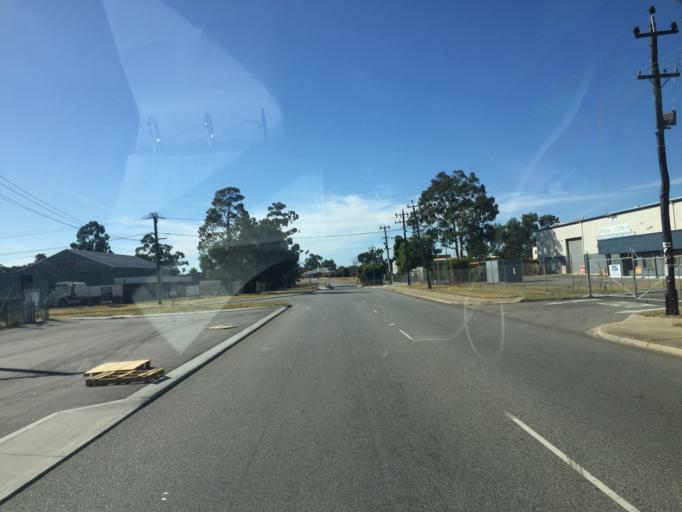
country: AU
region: Western Australia
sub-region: Gosnells
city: Maddington
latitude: -32.0420
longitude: 115.9854
